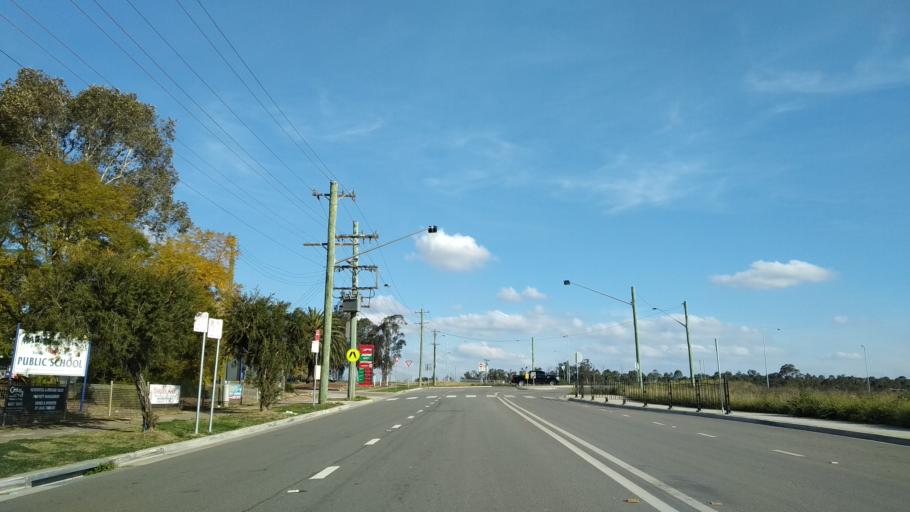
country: AU
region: New South Wales
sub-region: Blacktown
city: Riverstone
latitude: -33.6964
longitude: 150.8326
